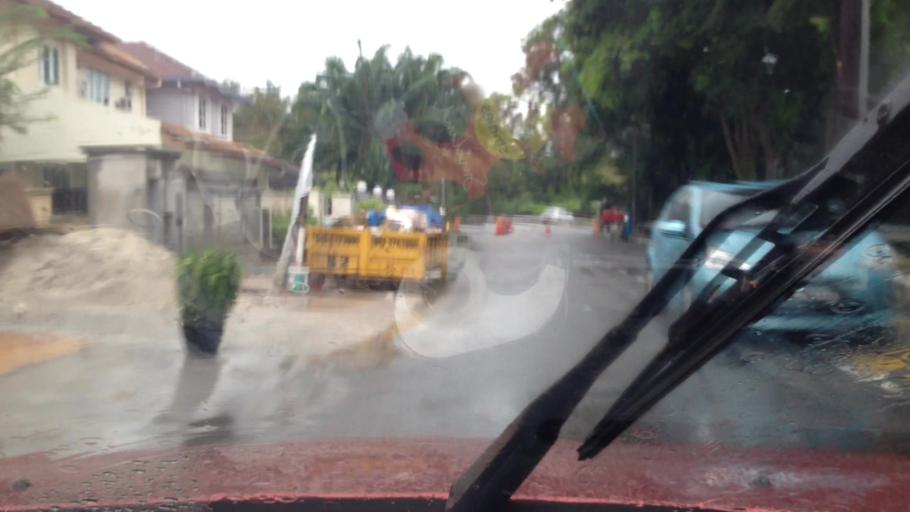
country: MY
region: Selangor
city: Subang Jaya
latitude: 3.0512
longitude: 101.5695
